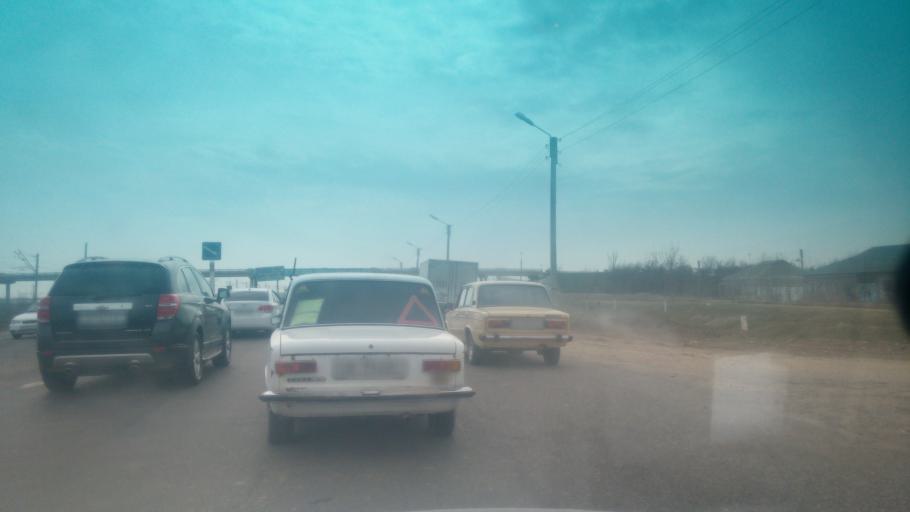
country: UZ
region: Sirdaryo
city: Guliston
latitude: 40.4726
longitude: 68.7705
